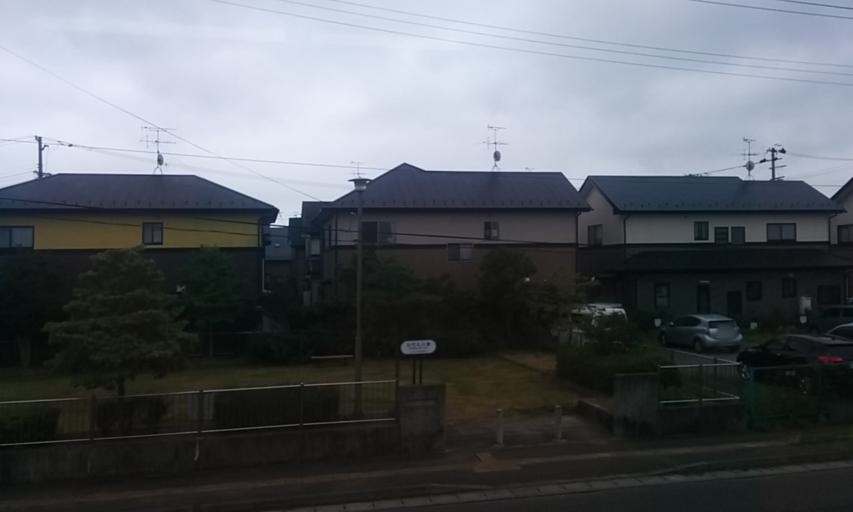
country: JP
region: Miyagi
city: Rifu
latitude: 38.2743
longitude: 140.9491
